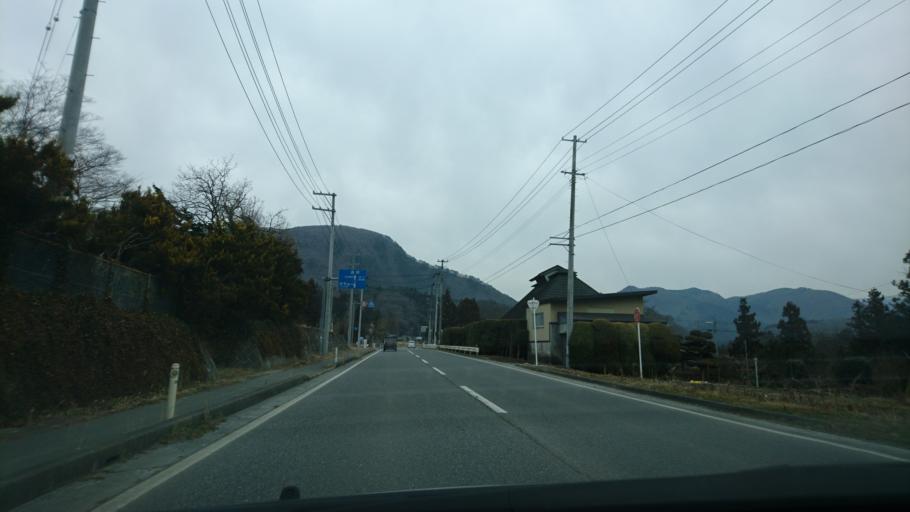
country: JP
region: Iwate
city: Tono
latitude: 39.1912
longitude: 141.5641
